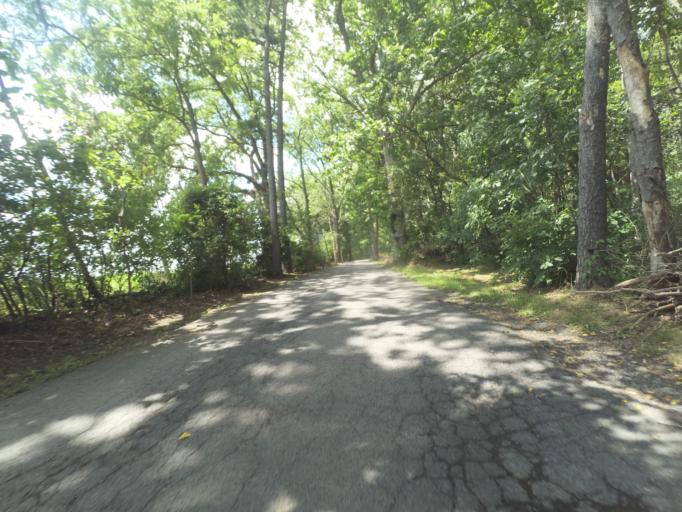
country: US
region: Pennsylvania
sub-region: Centre County
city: Boalsburg
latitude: 40.7833
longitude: -77.8168
